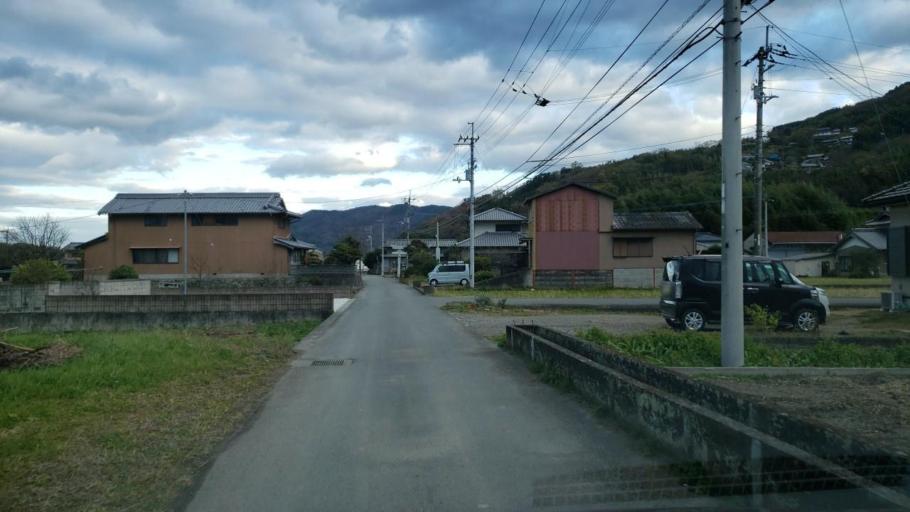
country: JP
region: Tokushima
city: Wakimachi
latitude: 34.0570
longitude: 134.1490
